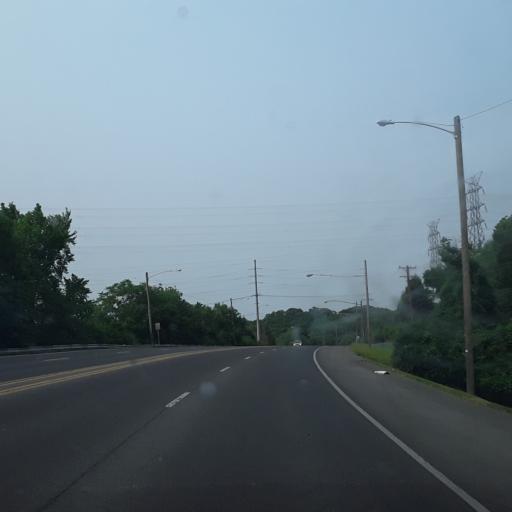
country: US
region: Tennessee
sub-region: Williamson County
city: Brentwood
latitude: 36.0573
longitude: -86.7747
